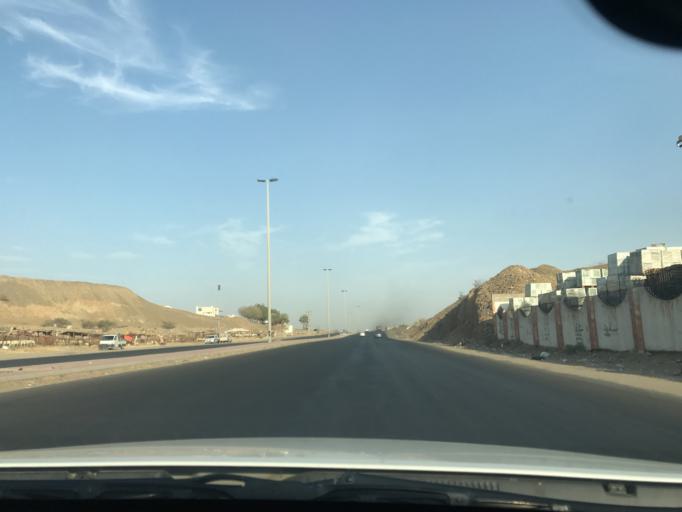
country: SA
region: Makkah
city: Jeddah
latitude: 21.4146
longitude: 39.4158
